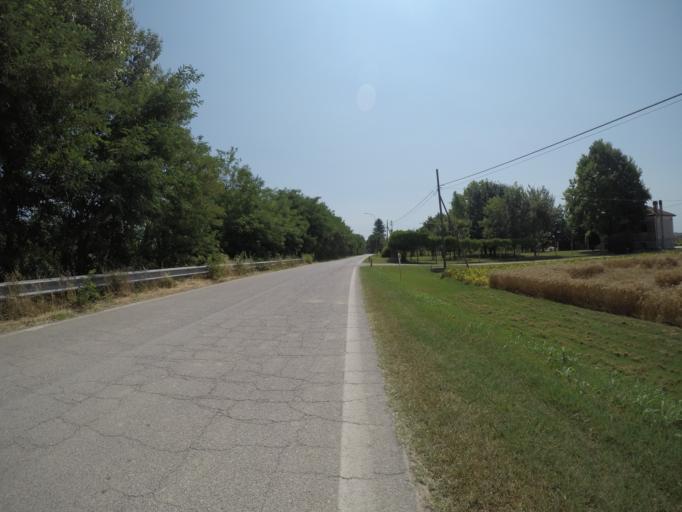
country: IT
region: Veneto
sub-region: Provincia di Rovigo
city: Pincara
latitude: 45.0021
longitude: 11.6375
